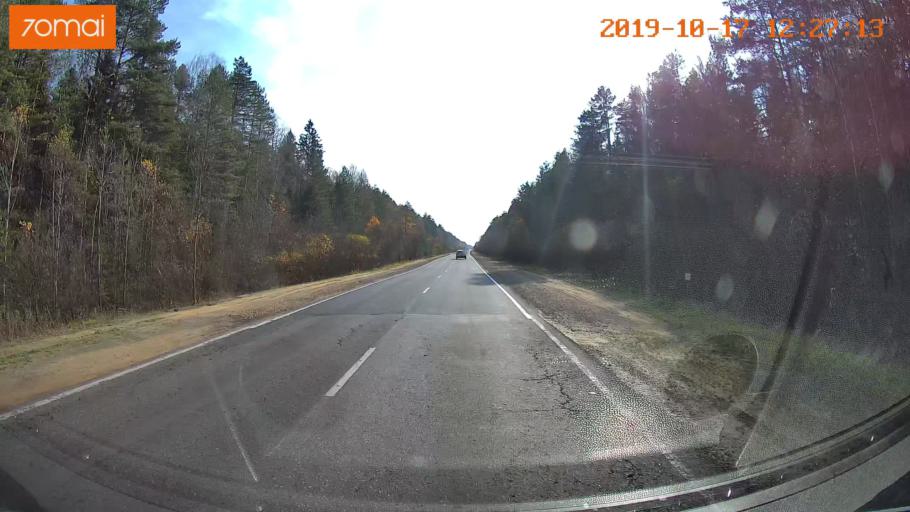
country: RU
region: Rjazan
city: Syntul
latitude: 55.0079
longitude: 41.2612
